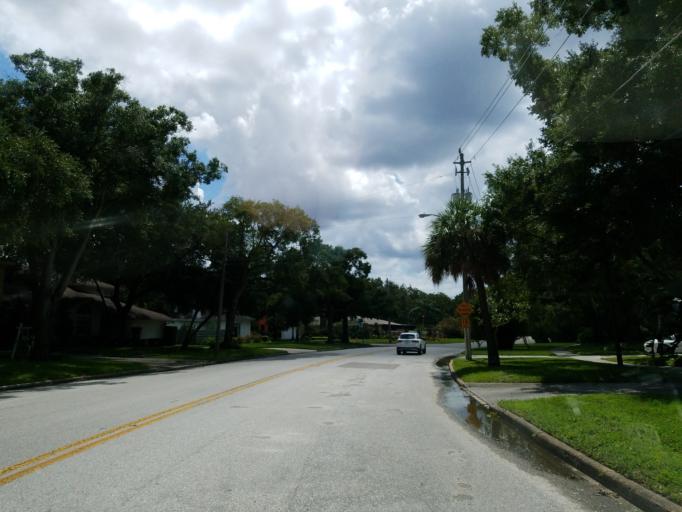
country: US
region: Florida
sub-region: Hillsborough County
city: Tampa
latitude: 27.9213
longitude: -82.4583
